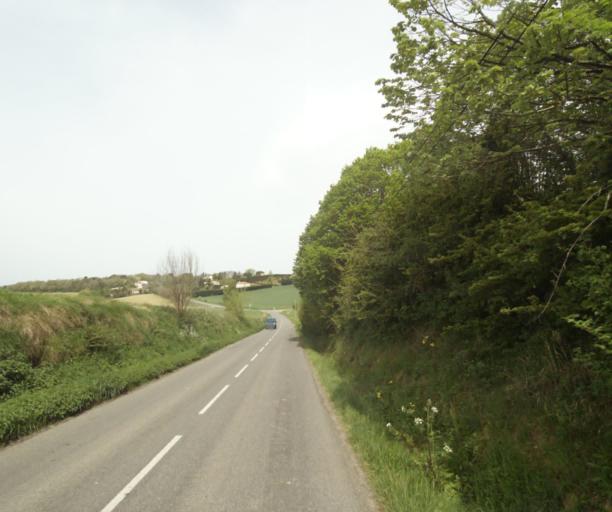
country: FR
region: Midi-Pyrenees
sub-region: Departement de la Haute-Garonne
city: Castanet-Tolosan
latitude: 43.4992
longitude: 1.4855
